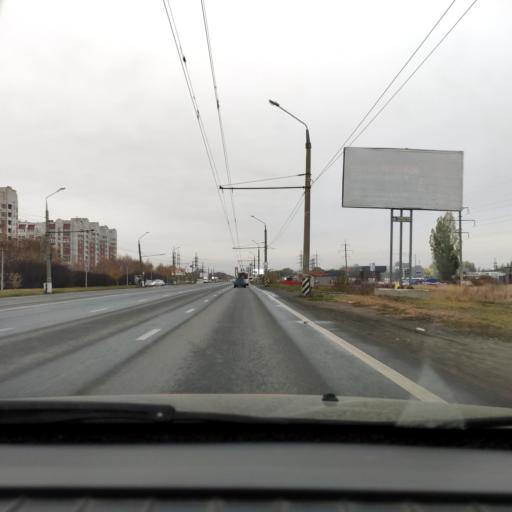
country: RU
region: Samara
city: Tol'yatti
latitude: 53.5500
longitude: 49.3266
